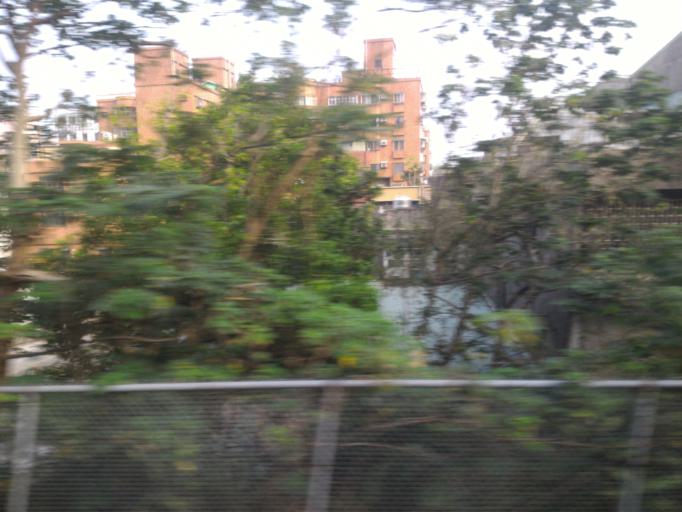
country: TW
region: Taiwan
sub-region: Taoyuan
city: Taoyuan
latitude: 24.9547
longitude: 121.3363
